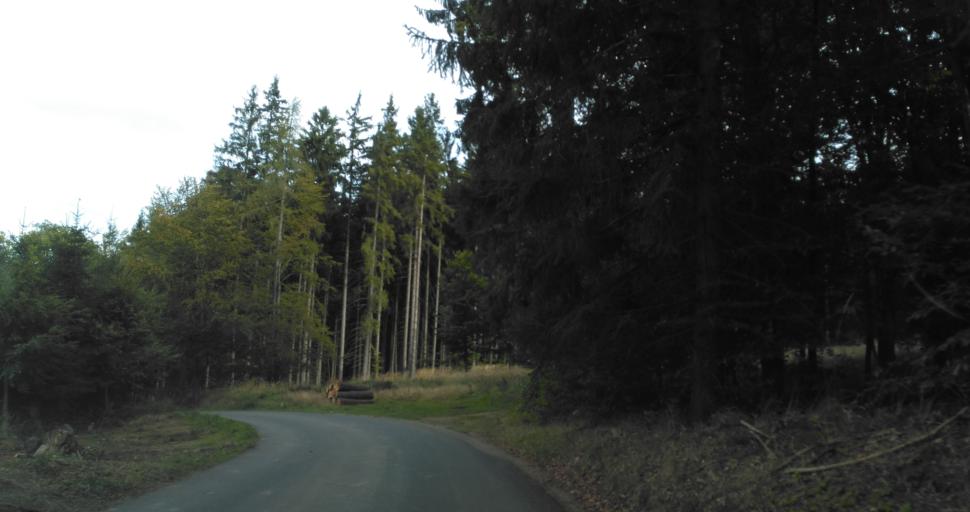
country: CZ
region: Plzensky
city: Zbiroh
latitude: 49.9282
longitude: 13.7934
